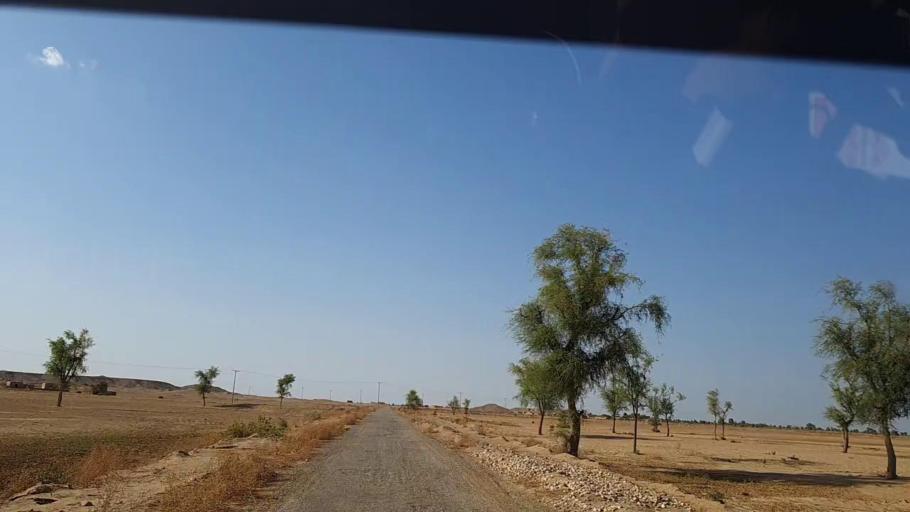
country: PK
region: Sindh
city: Johi
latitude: 26.5362
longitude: 67.5084
